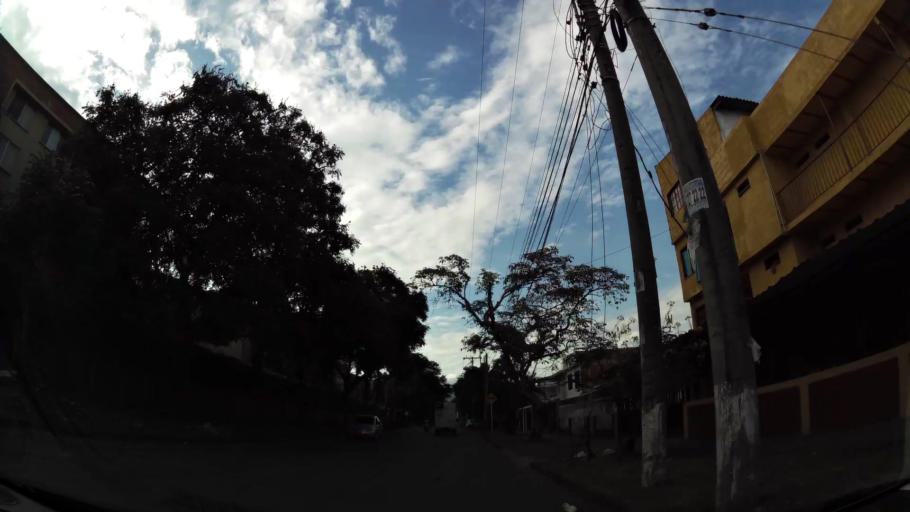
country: CO
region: Valle del Cauca
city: Cali
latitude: 3.4637
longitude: -76.5064
